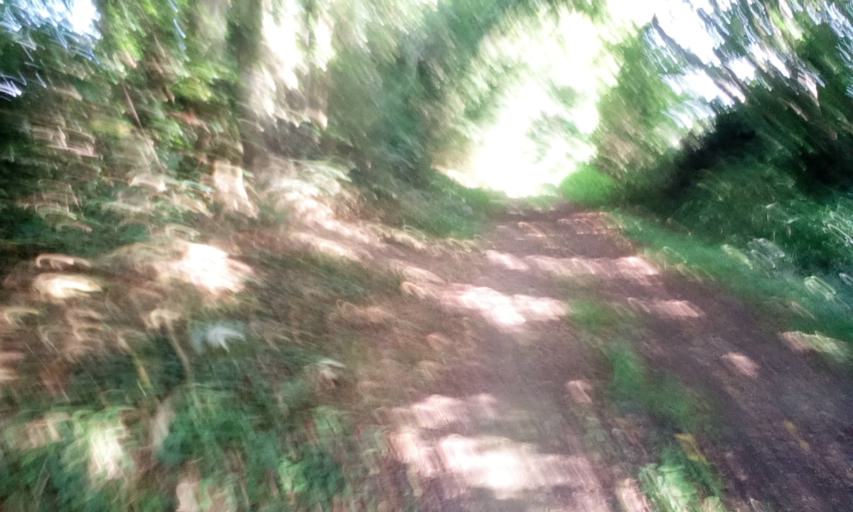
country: FR
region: Lower Normandy
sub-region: Departement du Calvados
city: Argences
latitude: 49.1271
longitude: -0.1428
